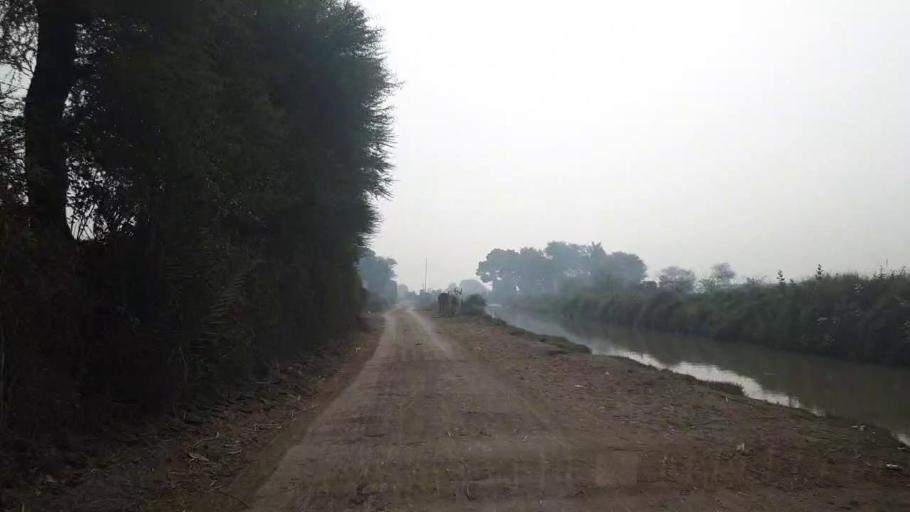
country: PK
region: Sindh
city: Tando Adam
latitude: 25.7560
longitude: 68.6156
